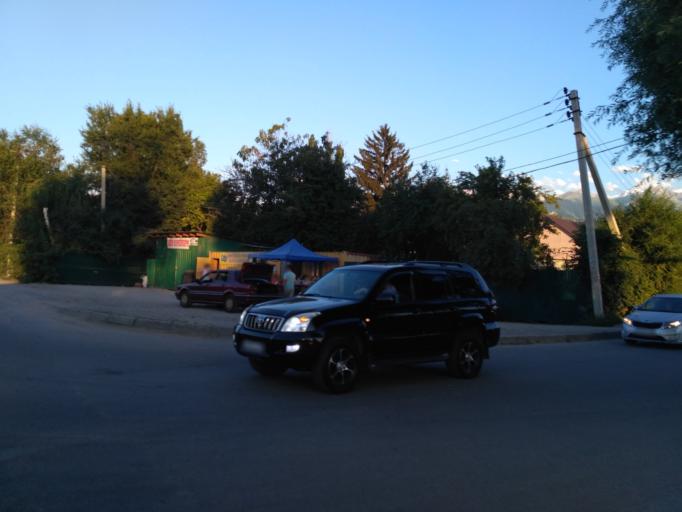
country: KZ
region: Almaty Qalasy
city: Almaty
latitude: 43.1776
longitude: 76.7549
